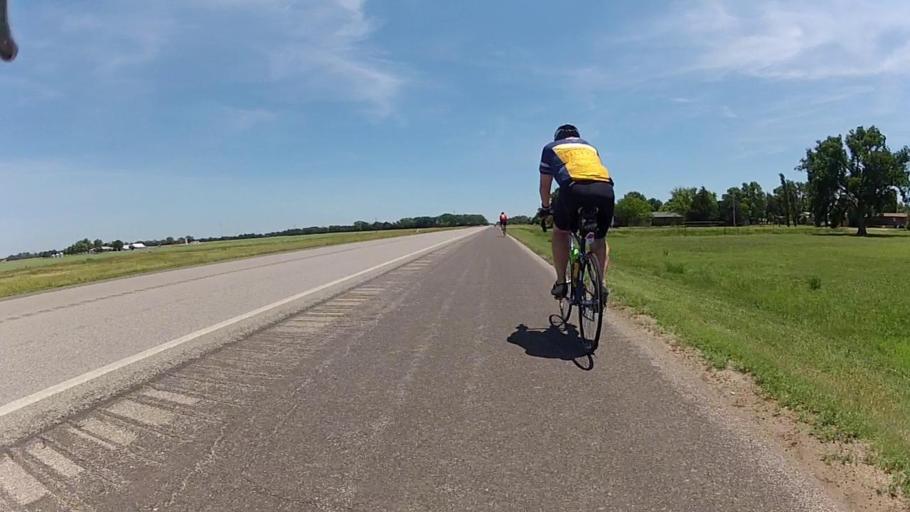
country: US
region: Kansas
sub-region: Barber County
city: Medicine Lodge
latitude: 37.2536
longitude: -98.4196
